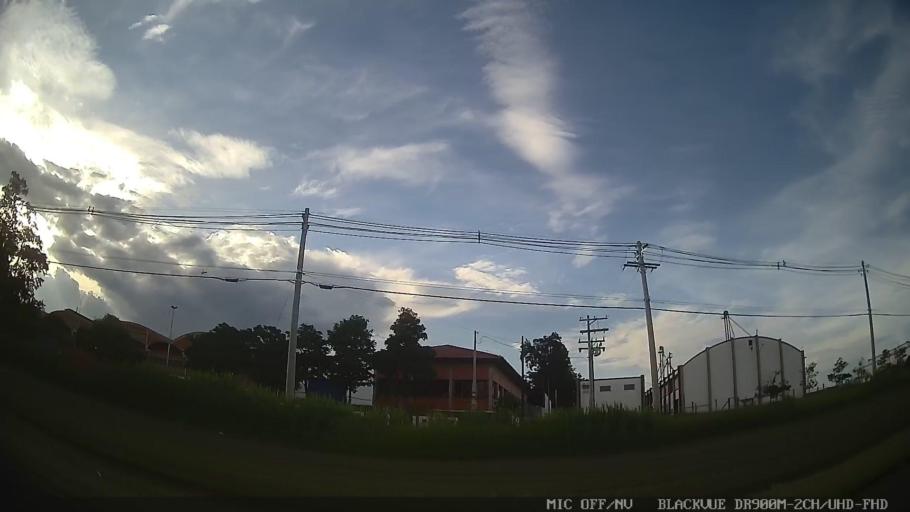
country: BR
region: Sao Paulo
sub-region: Tiete
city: Tiete
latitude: -23.0648
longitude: -47.7288
